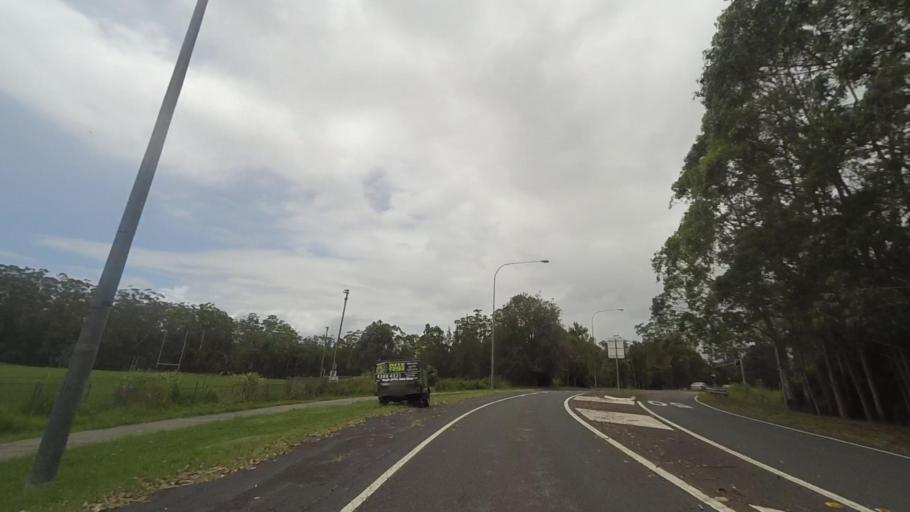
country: AU
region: New South Wales
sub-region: Wyong Shire
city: Berkeley Vale
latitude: -33.3422
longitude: 151.4275
